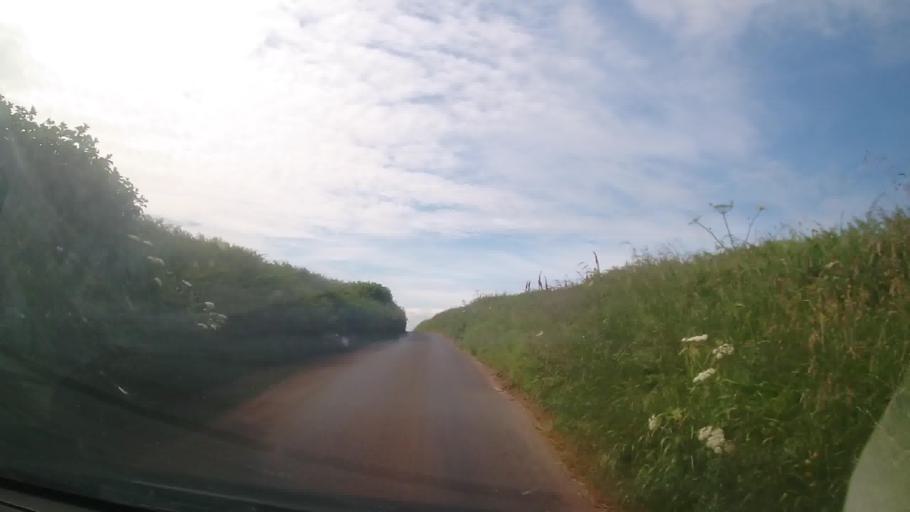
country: GB
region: England
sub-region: Devon
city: Salcombe
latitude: 50.2323
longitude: -3.6702
